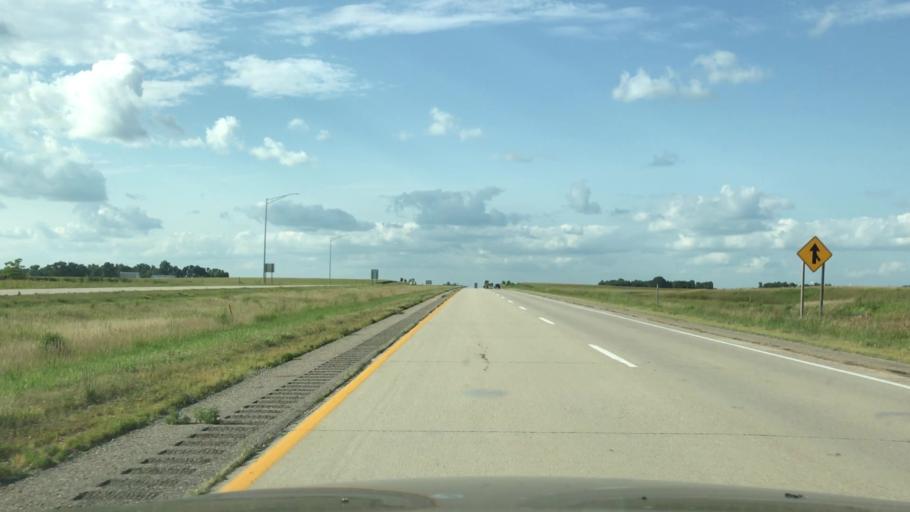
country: US
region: Iowa
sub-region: Osceola County
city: Sibley
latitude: 43.4075
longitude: -95.7170
